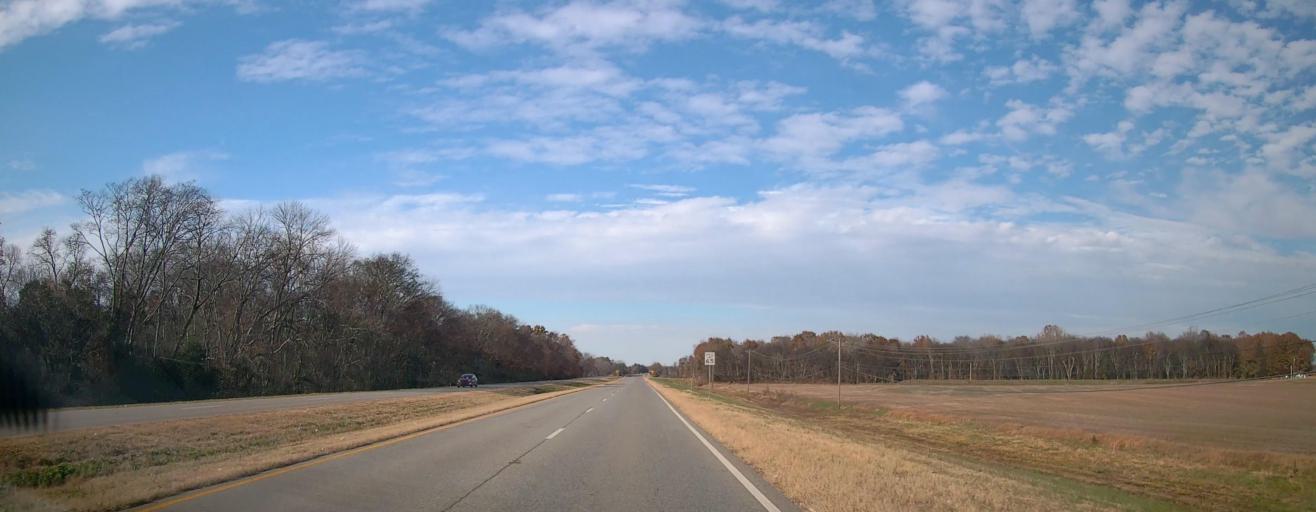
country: US
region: Alabama
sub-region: Morgan County
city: Decatur
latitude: 34.6844
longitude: -86.9512
